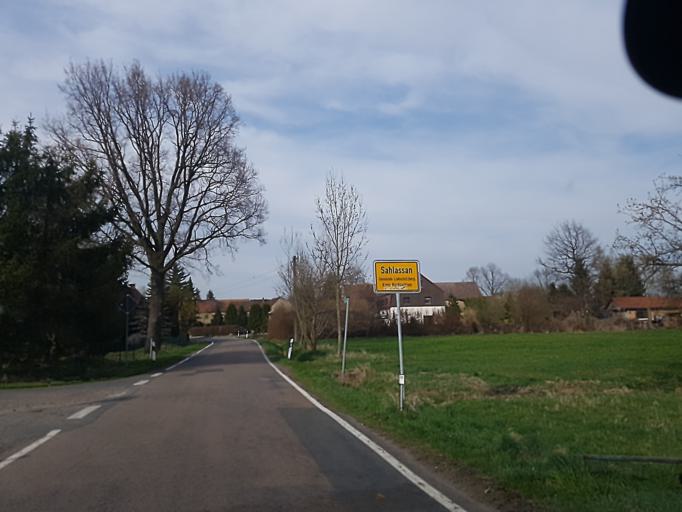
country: DE
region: Saxony
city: Strehla
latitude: 51.3656
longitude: 13.1933
